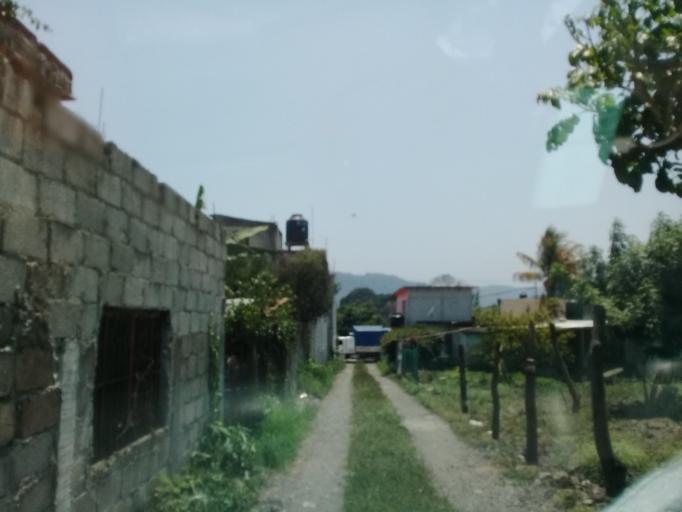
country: MX
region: Veracruz
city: Paraje Nuevo
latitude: 18.8682
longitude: -96.8752
